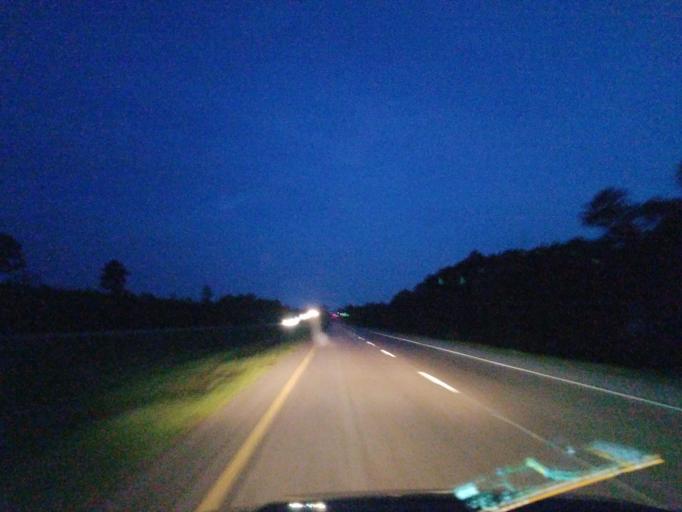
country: US
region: Mississippi
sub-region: Forrest County
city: Rawls Springs
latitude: 31.4809
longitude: -89.3240
